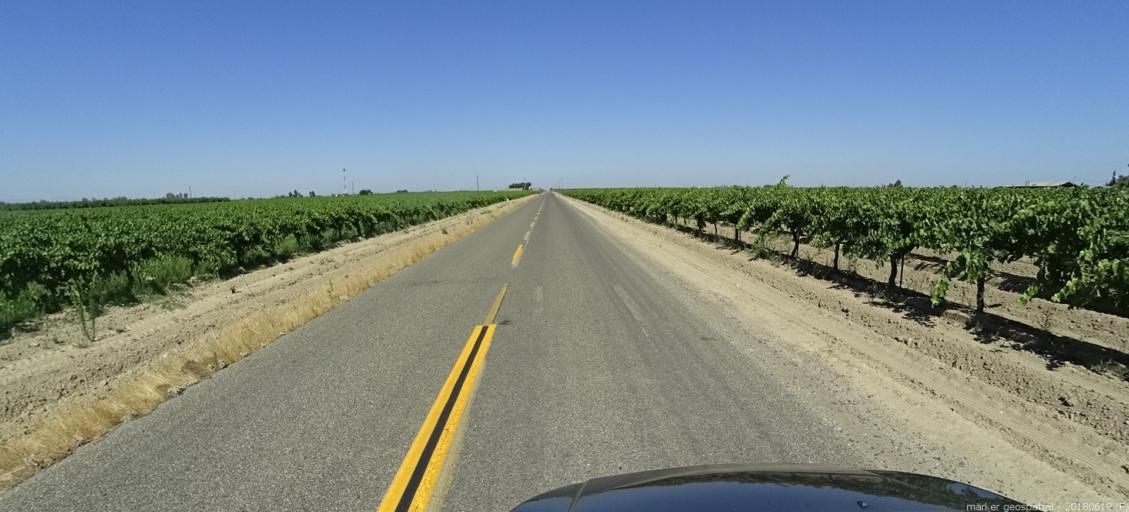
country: US
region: California
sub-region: Fresno County
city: Biola
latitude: 36.8368
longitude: -120.0433
